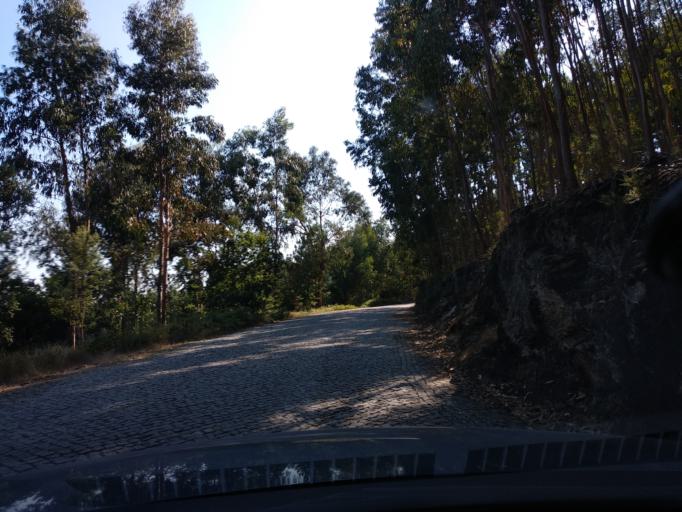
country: PT
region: Porto
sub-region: Paredes
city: Baltar
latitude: 41.2153
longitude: -8.3670
